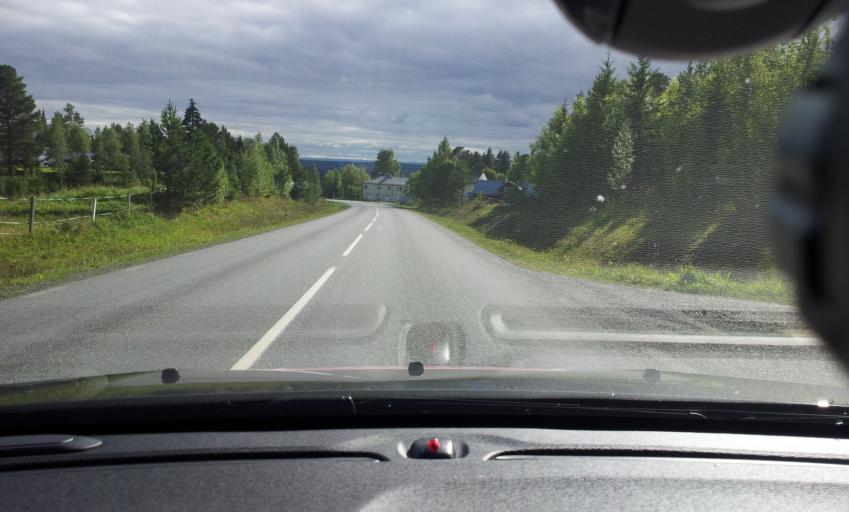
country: SE
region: Jaemtland
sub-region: Krokoms Kommun
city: Krokom
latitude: 63.4587
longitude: 14.1900
